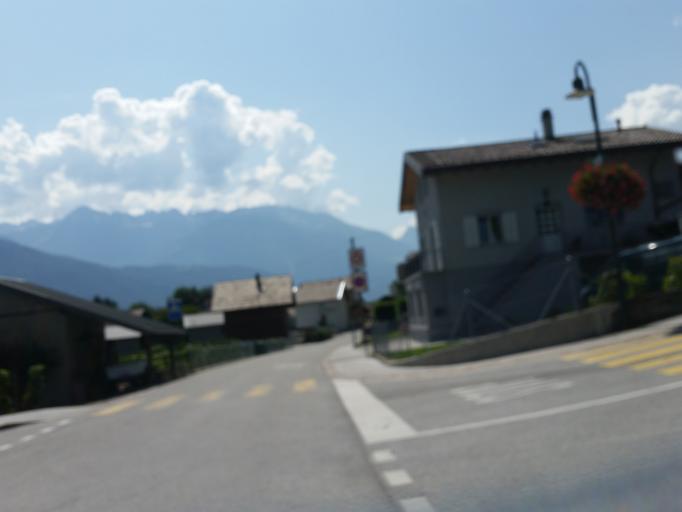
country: CH
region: Valais
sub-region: Martigny District
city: Fully
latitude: 46.1409
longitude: 7.1189
